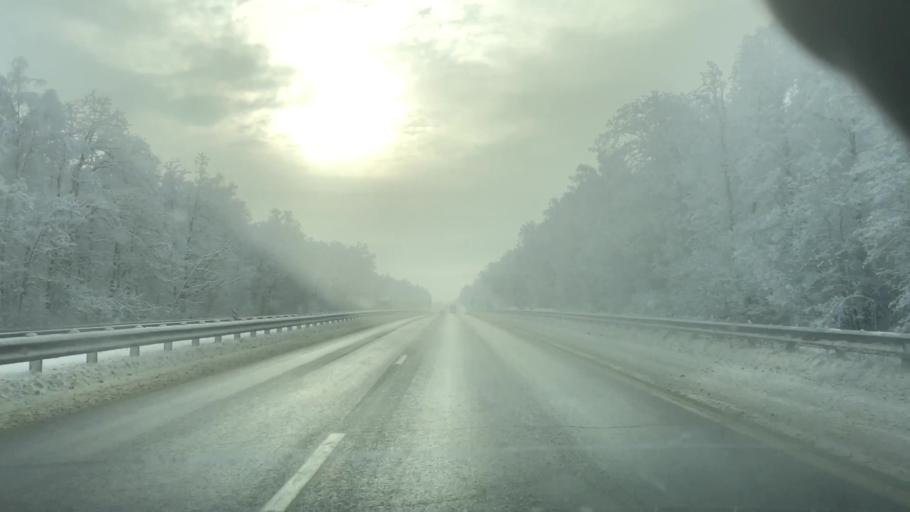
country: RU
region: Tula
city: Venev
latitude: 54.3667
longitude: 38.1547
